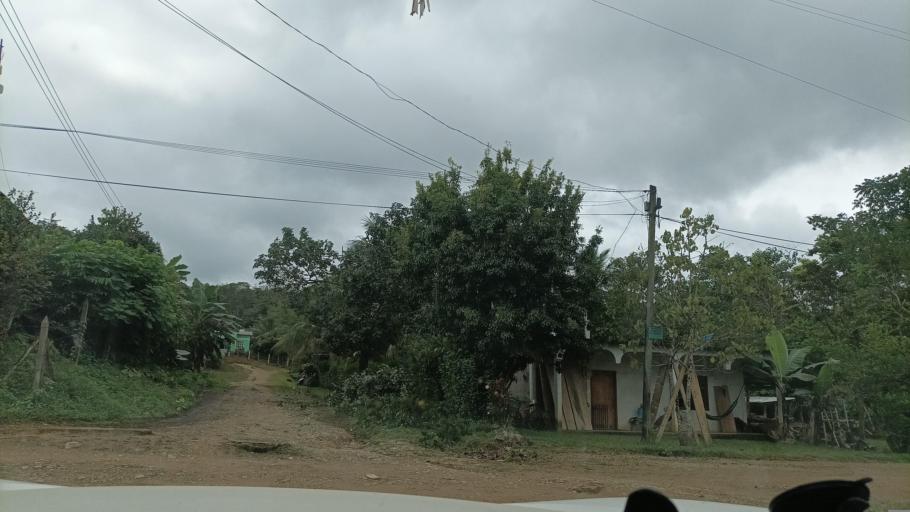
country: MX
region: Veracruz
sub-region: Uxpanapa
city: Poblado 10
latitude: 17.2688
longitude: -94.4996
